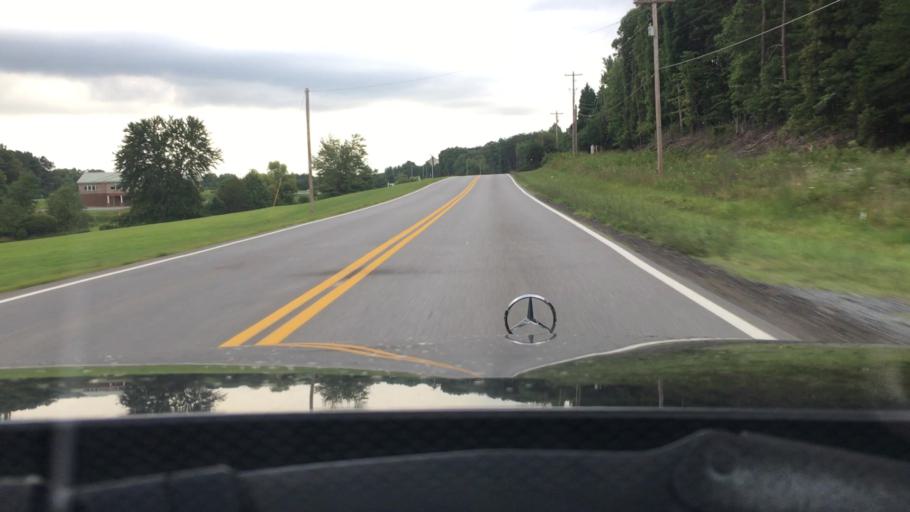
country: US
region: Virginia
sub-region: Campbell County
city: Timberlake
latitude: 37.3215
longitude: -79.2335
